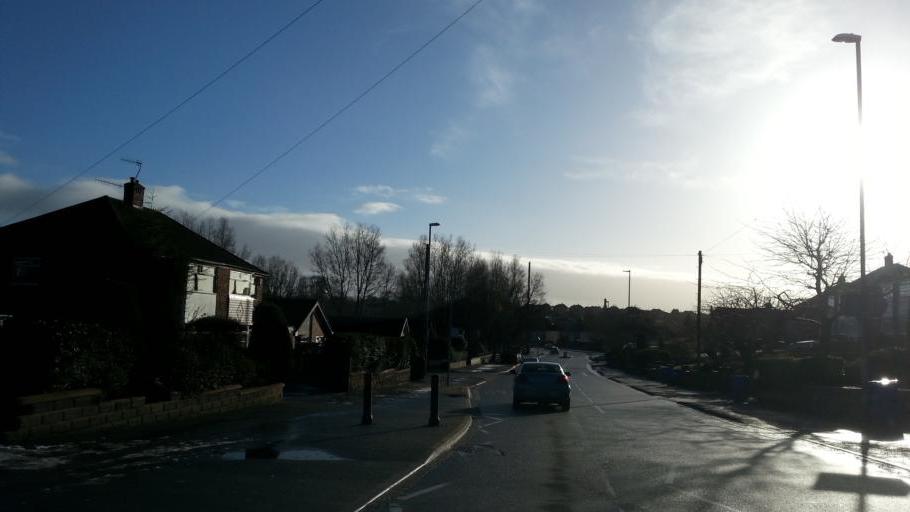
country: GB
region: England
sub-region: Staffordshire
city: Longton
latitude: 52.9846
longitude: -2.1584
